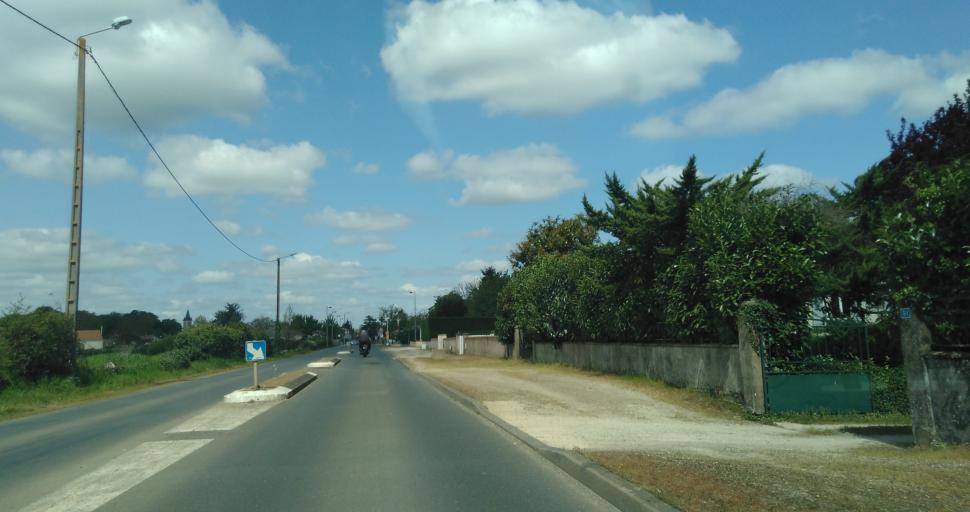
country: FR
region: Poitou-Charentes
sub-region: Departement des Deux-Sevres
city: Villiers-en-Plaine
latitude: 46.4043
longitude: -0.5314
